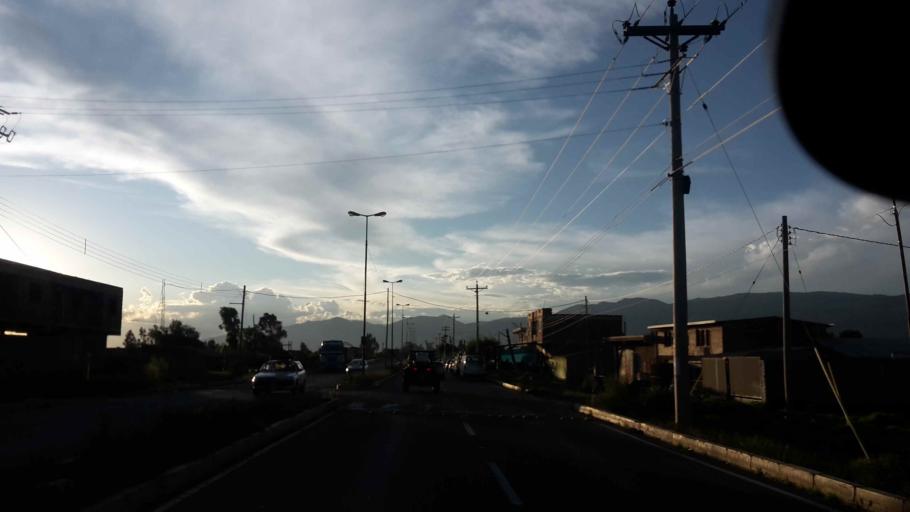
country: BO
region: Cochabamba
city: Punata
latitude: -17.5553
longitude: -65.8120
